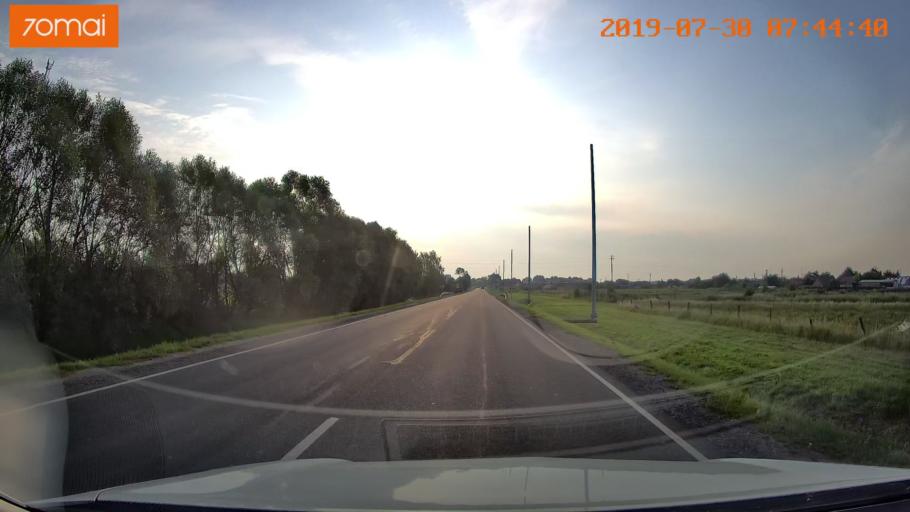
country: RU
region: Kaliningrad
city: Gvardeysk
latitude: 54.6503
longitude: 21.3311
